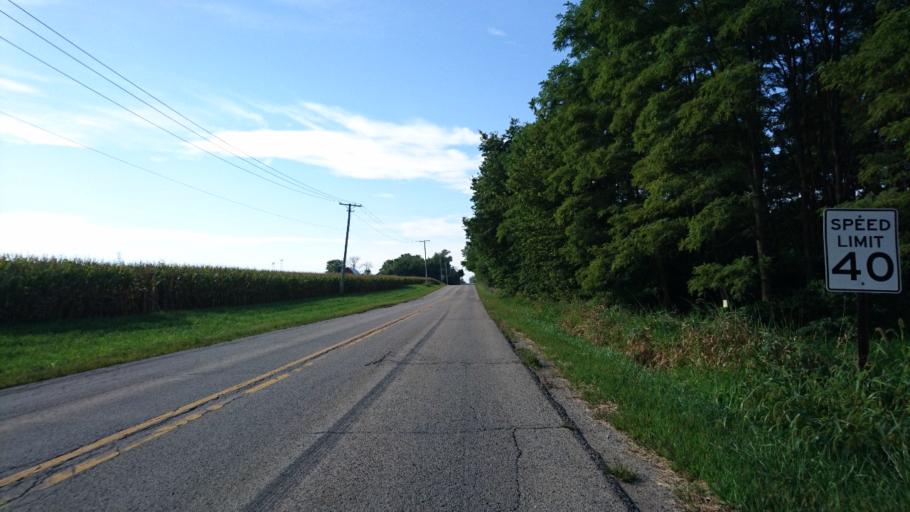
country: US
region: Illinois
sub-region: Will County
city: Ingalls Park
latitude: 41.4959
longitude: -88.0231
